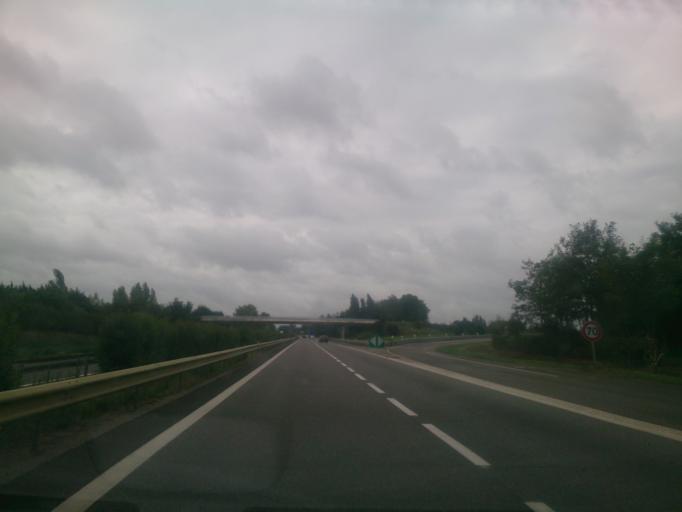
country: FR
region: Midi-Pyrenees
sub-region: Departement de la Haute-Garonne
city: Noe
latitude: 43.3705
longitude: 1.2755
